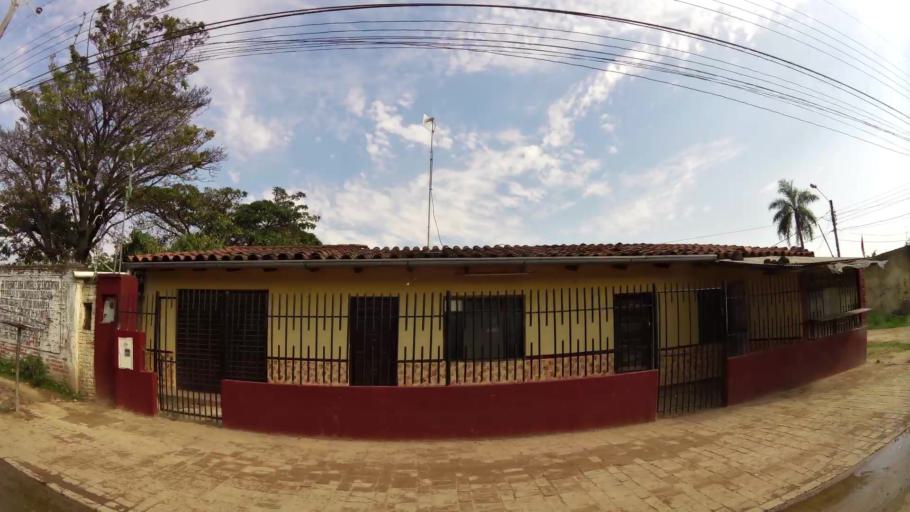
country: BO
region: Santa Cruz
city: Santa Cruz de la Sierra
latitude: -17.7208
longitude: -63.1363
